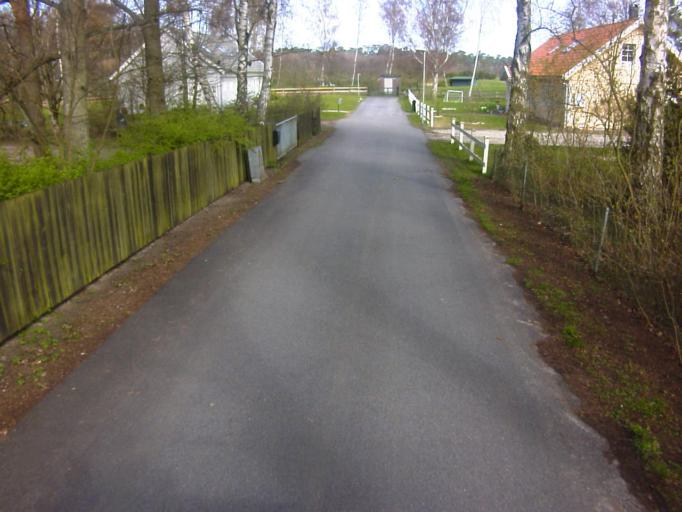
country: SE
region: Skane
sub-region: Kavlinge Kommun
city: Hofterup
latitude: 55.7922
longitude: 12.9594
